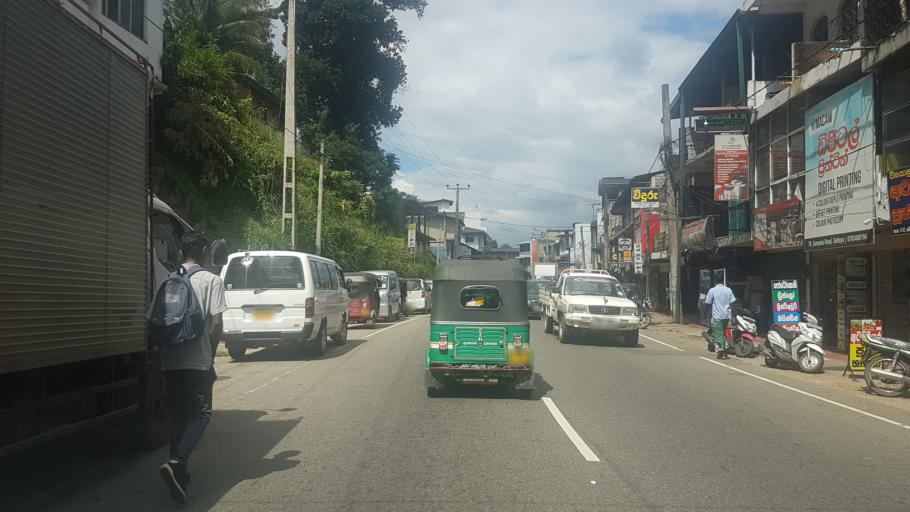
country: LK
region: Central
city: Gampola
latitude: 7.2134
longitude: 80.5986
